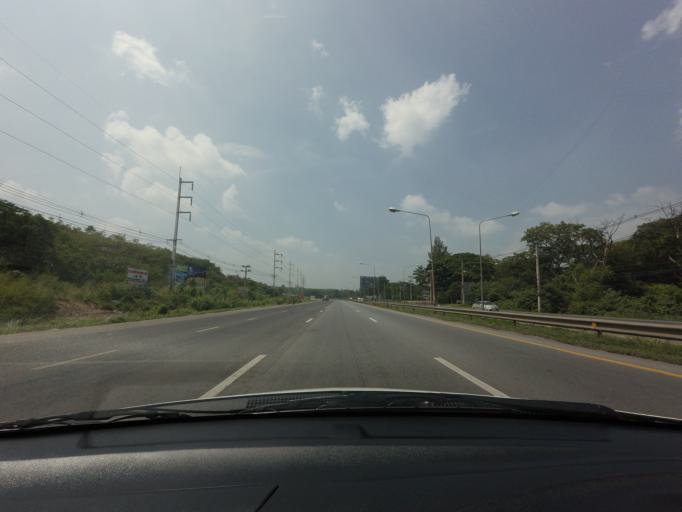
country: TH
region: Nakhon Ratchasima
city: Pak Chong
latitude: 14.6576
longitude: 101.3735
